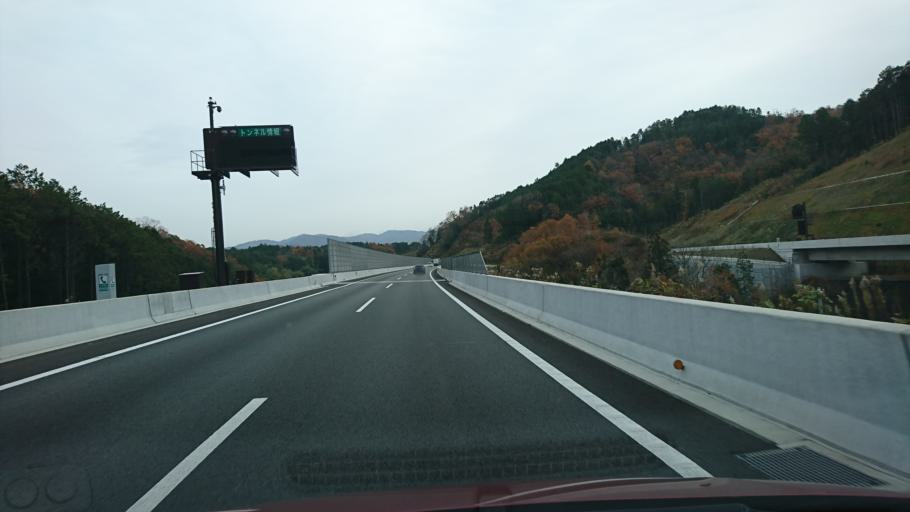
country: JP
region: Hyogo
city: Takarazuka
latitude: 34.8886
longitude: 135.3542
